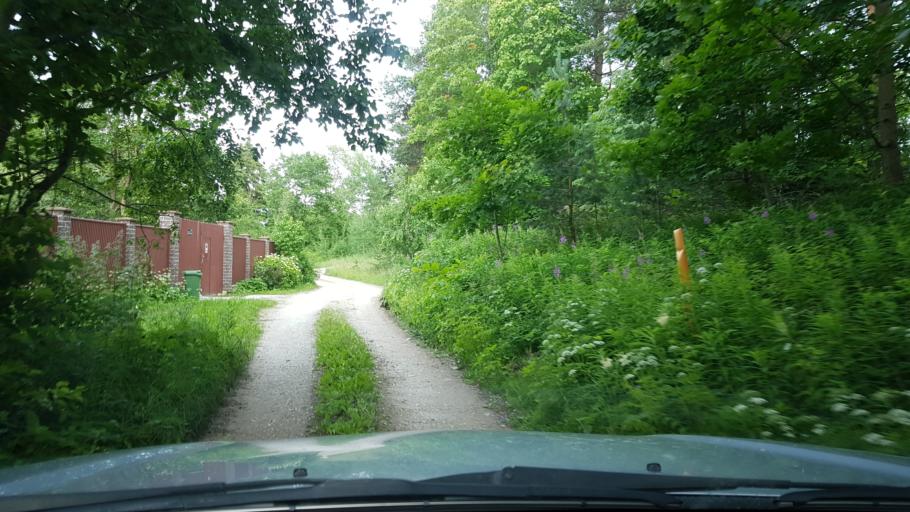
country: EE
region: Ida-Virumaa
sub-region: Narva-Joesuu linn
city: Narva-Joesuu
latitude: 59.4533
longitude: 28.0775
